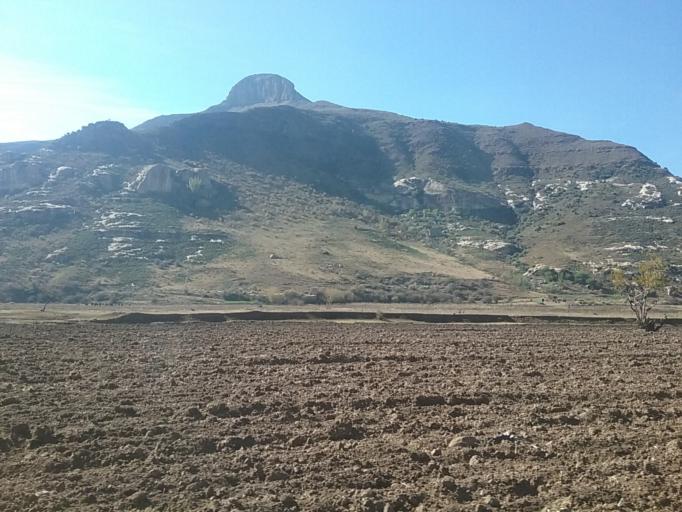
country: LS
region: Berea
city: Teyateyaneng
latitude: -29.2485
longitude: 27.9088
